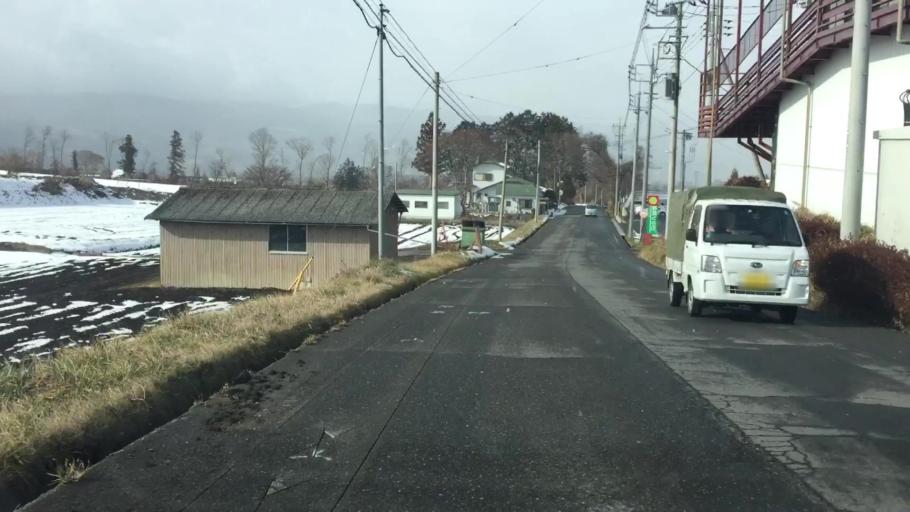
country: JP
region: Gunma
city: Numata
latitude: 36.6077
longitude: 139.0877
